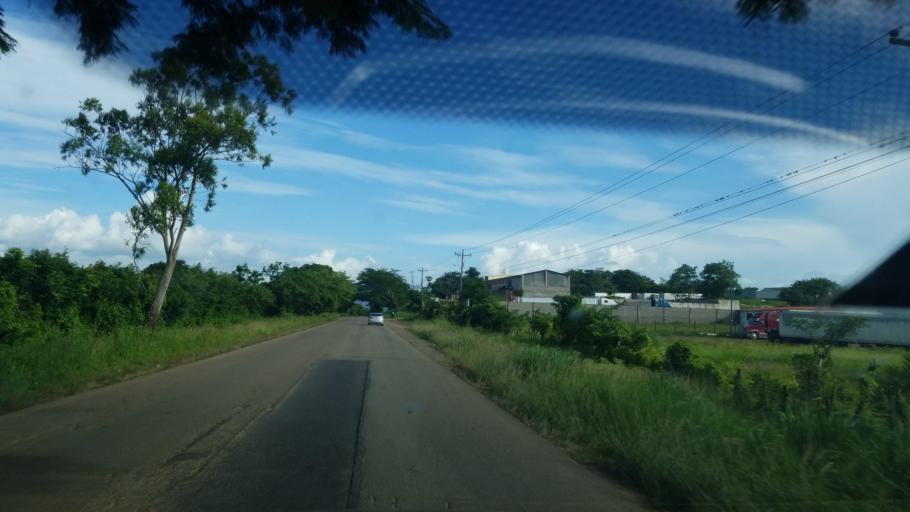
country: HN
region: El Paraiso
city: Arauli
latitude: 13.9501
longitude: -86.5605
